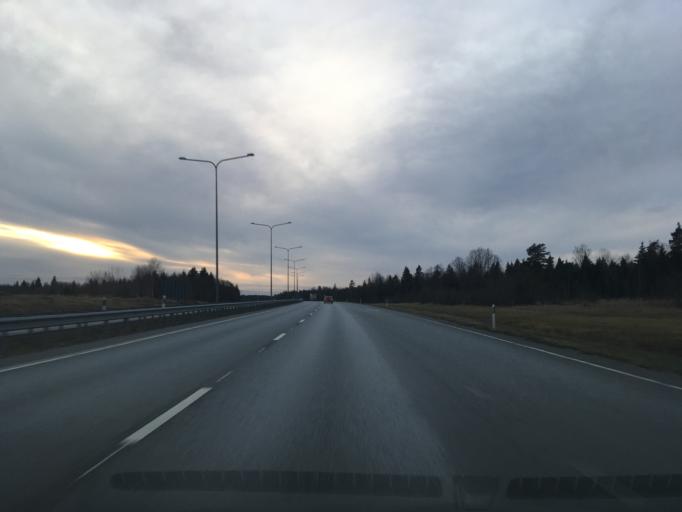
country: EE
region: Laeaene-Virumaa
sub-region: Kadrina vald
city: Kadrina
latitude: 59.4624
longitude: 25.9958
